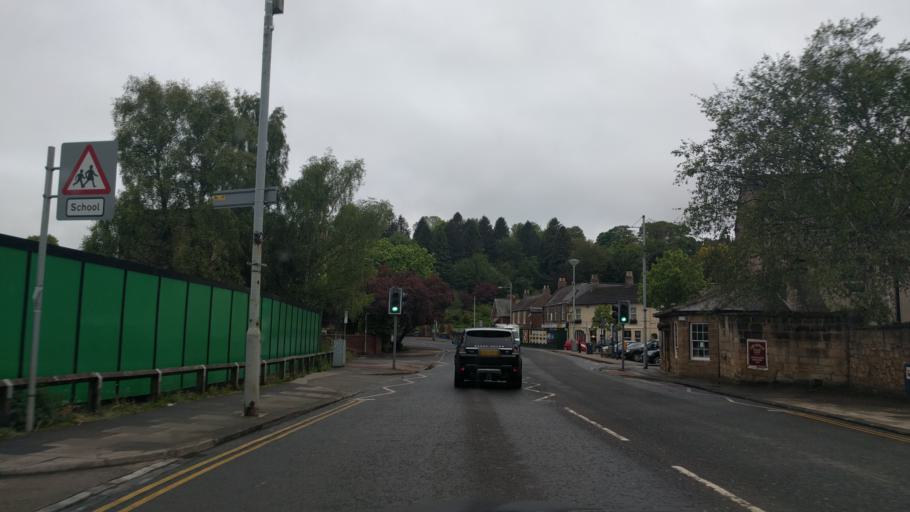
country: GB
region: England
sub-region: Northumberland
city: Morpeth
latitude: 55.1662
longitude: -1.6863
